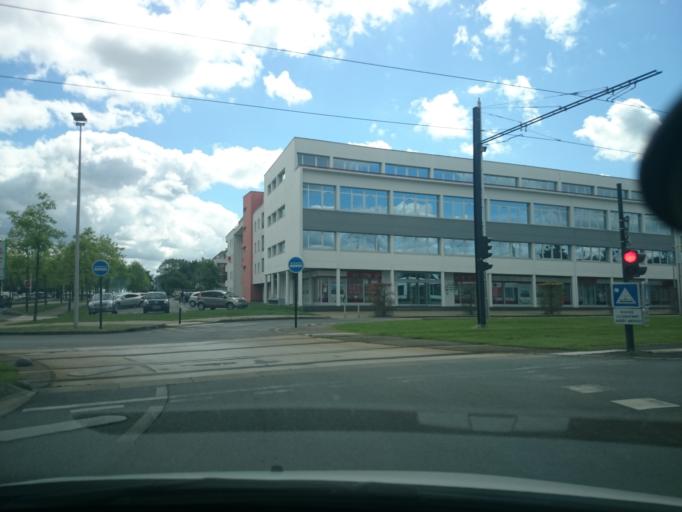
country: FR
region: Pays de la Loire
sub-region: Departement de la Loire-Atlantique
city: Saint-Herblain
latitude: 47.2221
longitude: -1.6370
